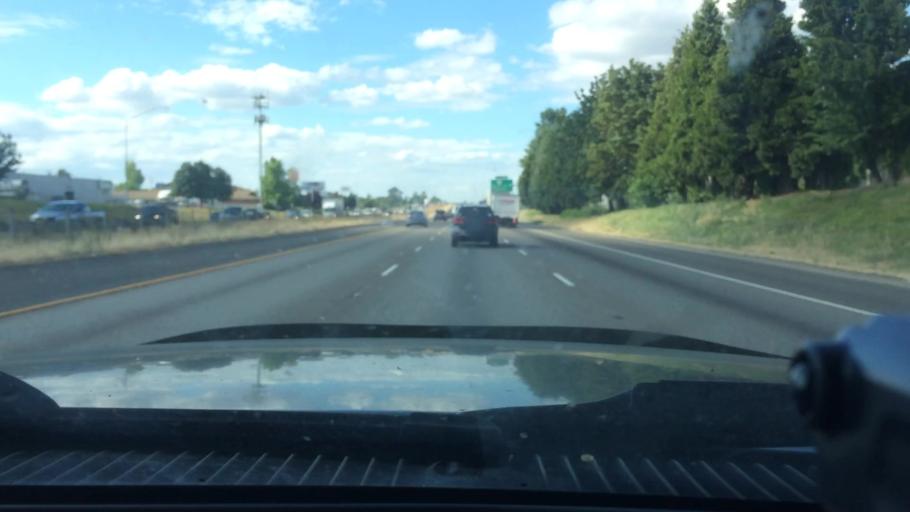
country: US
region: Oregon
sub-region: Marion County
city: Four Corners
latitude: 44.9435
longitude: -122.9902
